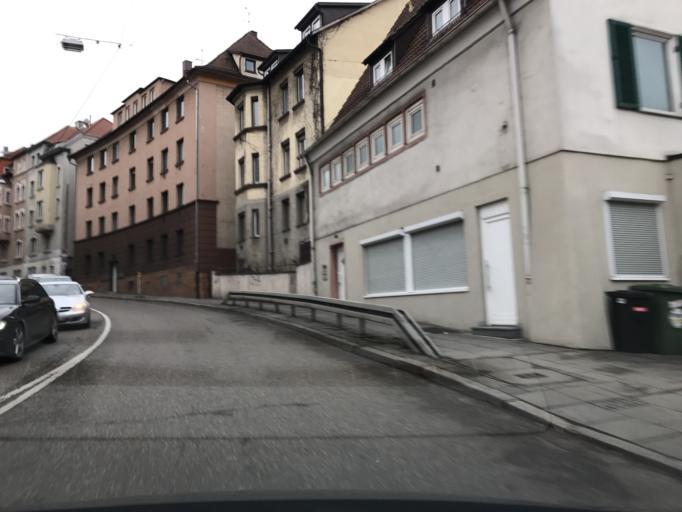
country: DE
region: Baden-Wuerttemberg
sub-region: Regierungsbezirk Stuttgart
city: Stuttgart-Ost
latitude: 48.7800
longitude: 9.2012
